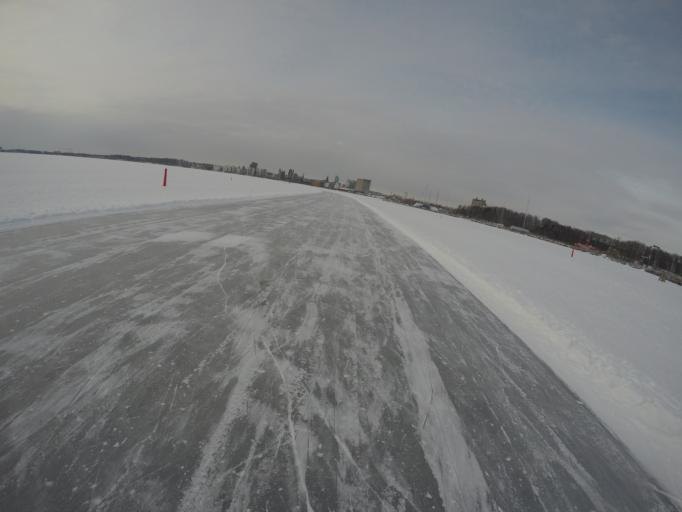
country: SE
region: Vaestmanland
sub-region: Vasteras
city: Vasteras
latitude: 59.5987
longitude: 16.5723
